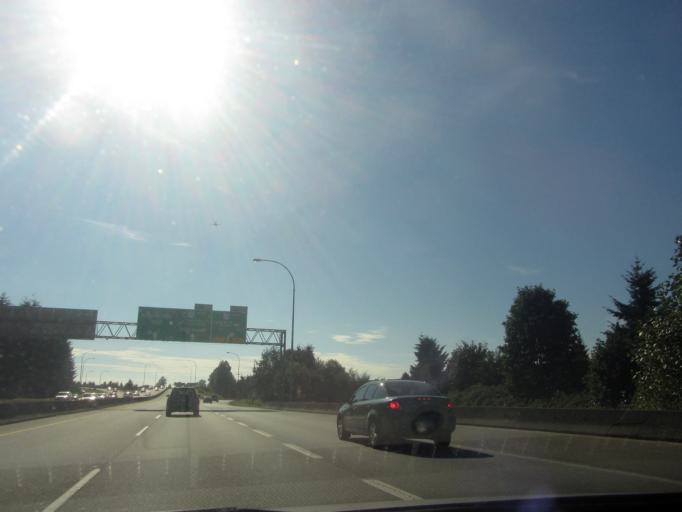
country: CA
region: British Columbia
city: Richmond
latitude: 49.1775
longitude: -123.0846
